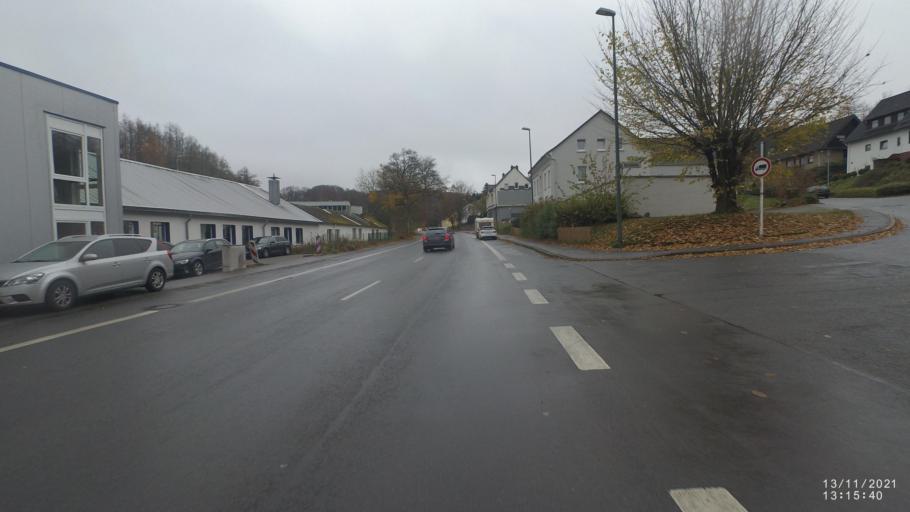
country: DE
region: North Rhine-Westphalia
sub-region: Regierungsbezirk Arnsberg
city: Luedenscheid
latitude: 51.2431
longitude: 7.6224
